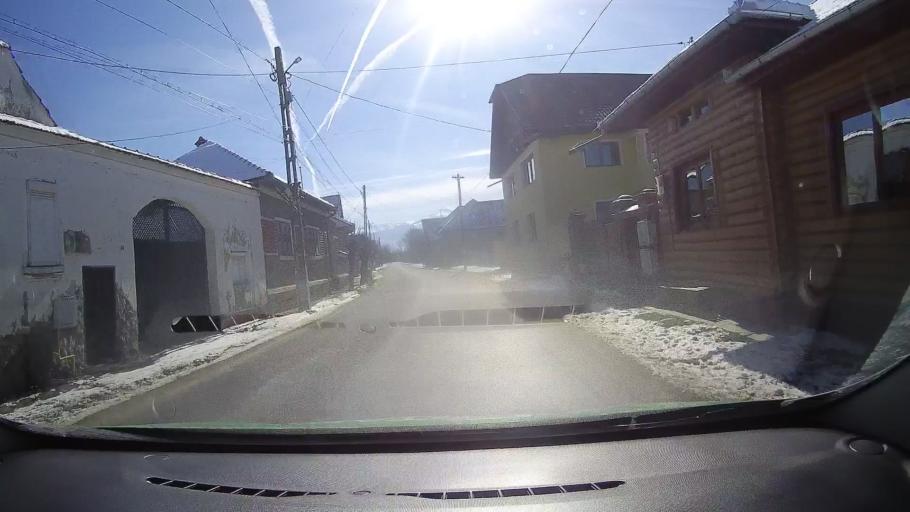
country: RO
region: Brasov
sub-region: Comuna Sambata de Sus
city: Sambata de Sus
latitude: 45.7566
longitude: 24.8307
